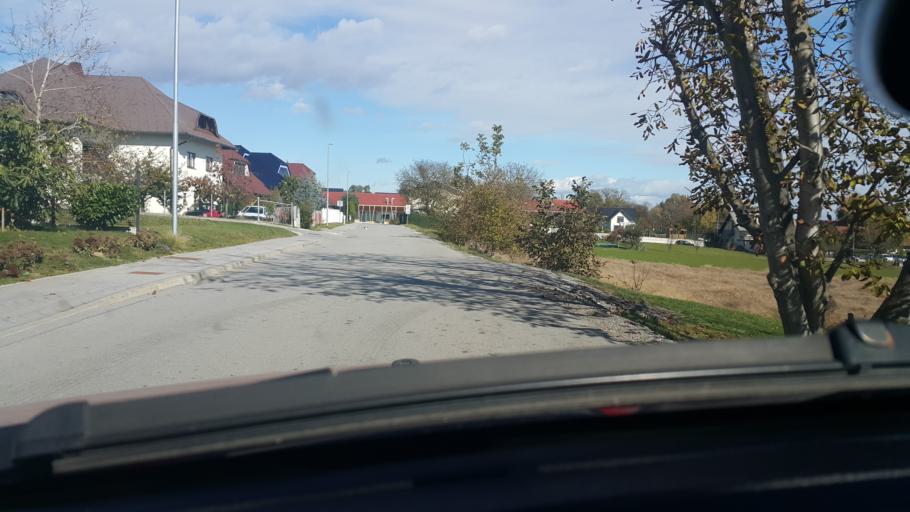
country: SI
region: Race-Fram
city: Fram
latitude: 46.4487
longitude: 15.6358
